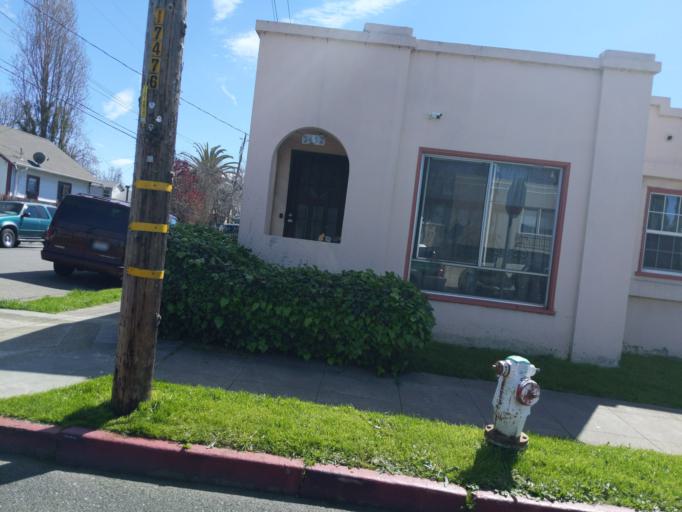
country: US
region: California
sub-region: Alameda County
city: Piedmont
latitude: 37.7902
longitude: -122.1989
